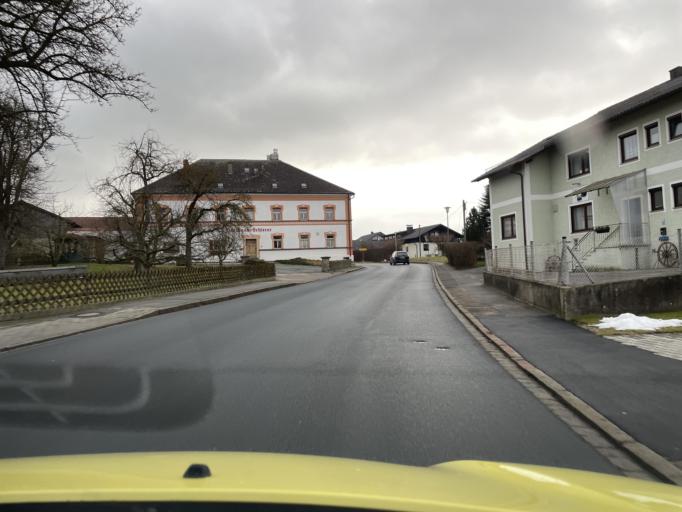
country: DE
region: Bavaria
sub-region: Upper Palatinate
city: Zandt
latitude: 49.1684
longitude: 12.6981
